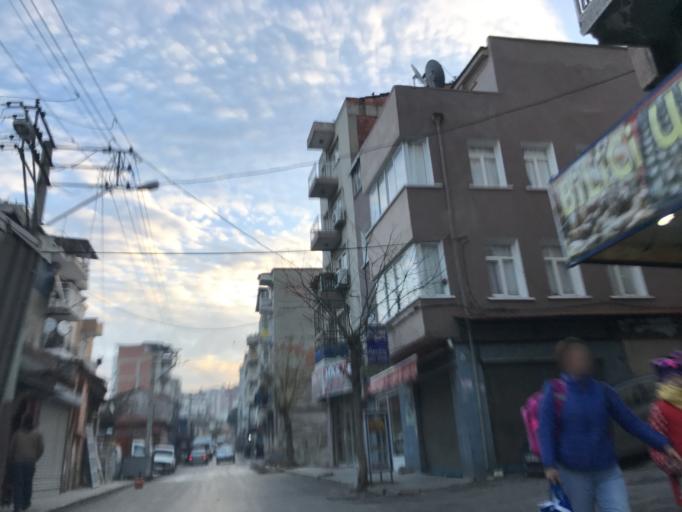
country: TR
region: Izmir
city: Izmir
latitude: 38.4104
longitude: 27.1320
